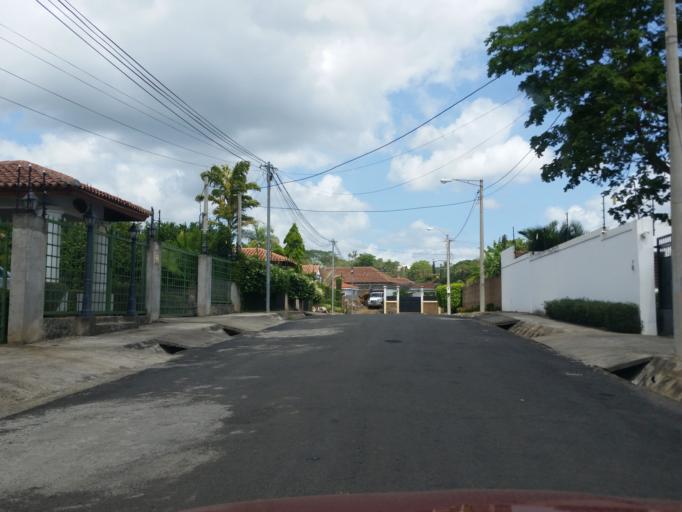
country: NI
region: Managua
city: Managua
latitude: 12.0746
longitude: -86.2355
